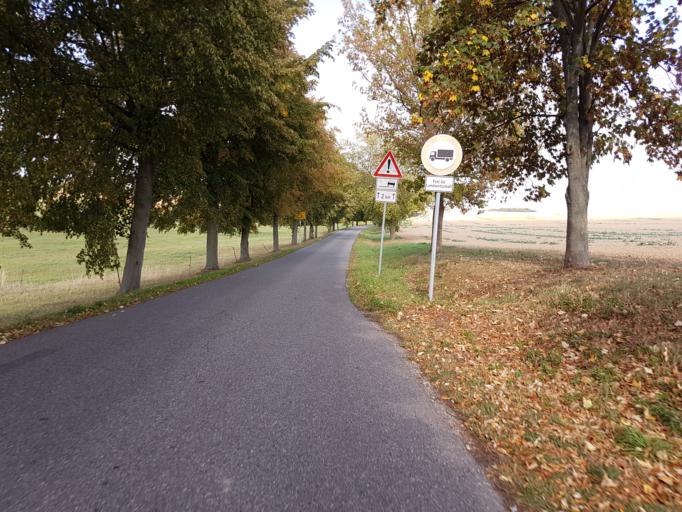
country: DE
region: Saxony
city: Claussnitz
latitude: 50.9724
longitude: 12.8861
